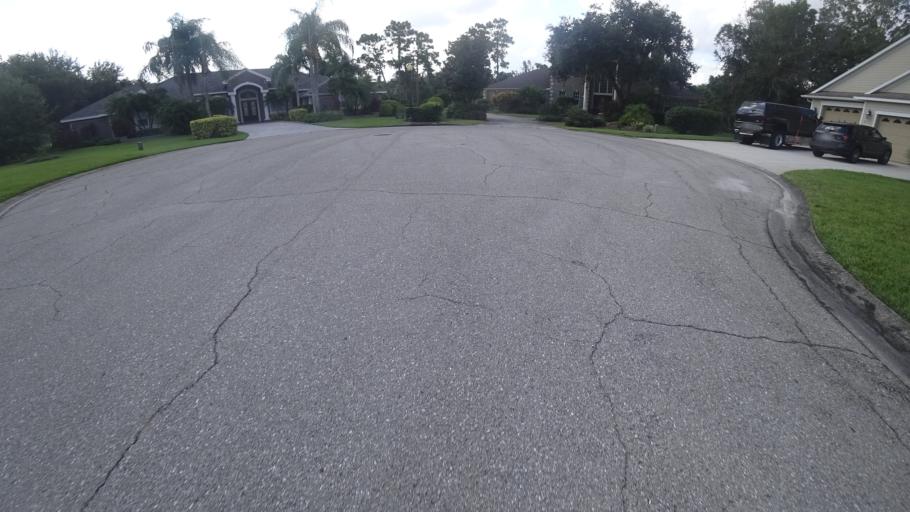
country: US
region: Florida
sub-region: Sarasota County
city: The Meadows
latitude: 27.4198
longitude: -82.4380
